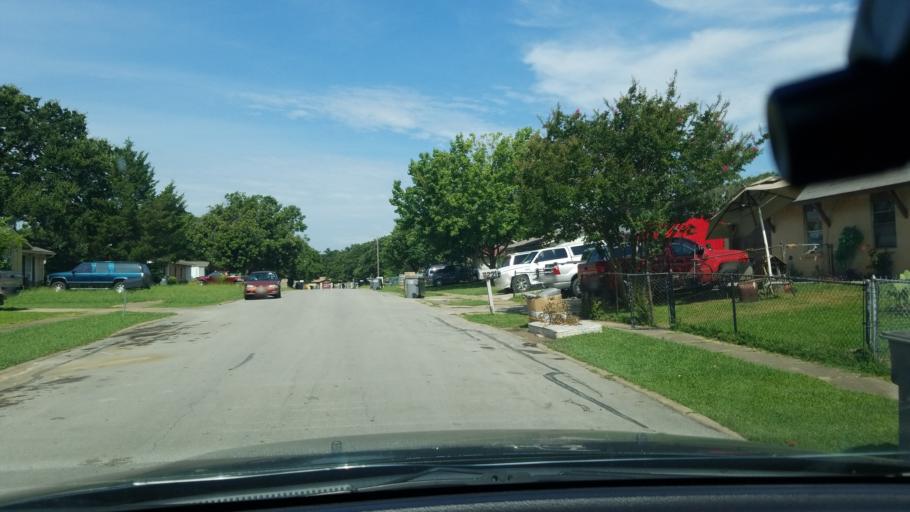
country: US
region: Texas
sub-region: Dallas County
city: Balch Springs
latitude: 32.7264
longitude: -96.6321
